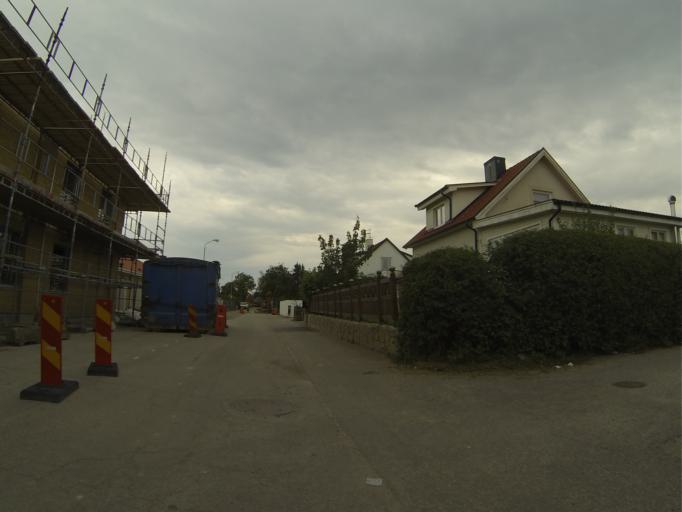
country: SE
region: Skane
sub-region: Staffanstorps Kommun
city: Staffanstorp
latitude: 55.6505
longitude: 13.2063
